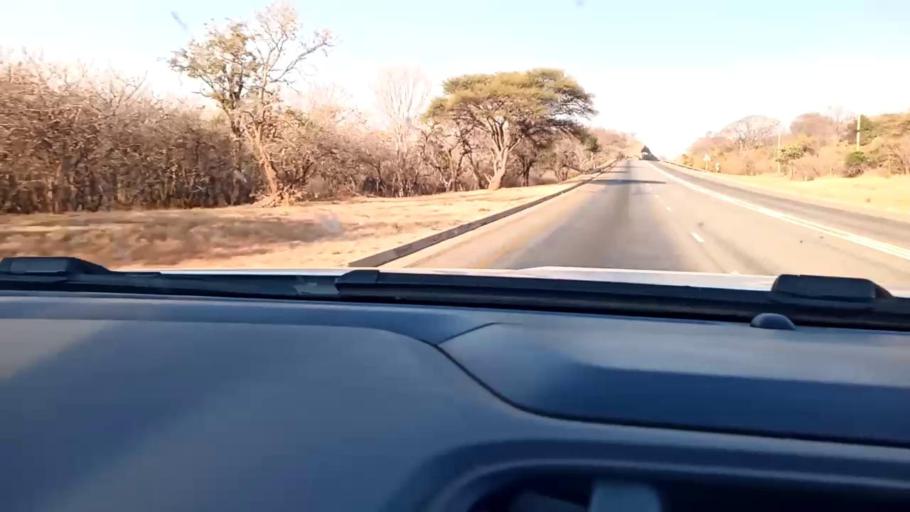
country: ZA
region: Limpopo
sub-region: Mopani District Municipality
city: Duiwelskloof
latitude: -23.6368
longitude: 30.1450
